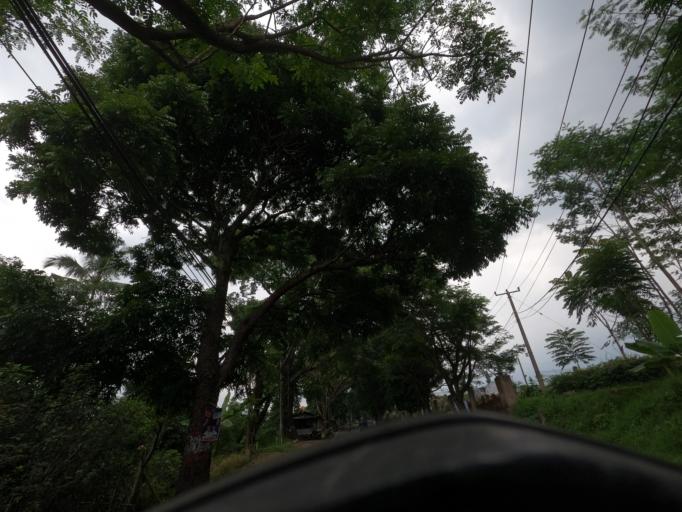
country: ID
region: West Java
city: Sukabumi
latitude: -6.7903
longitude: 107.0683
